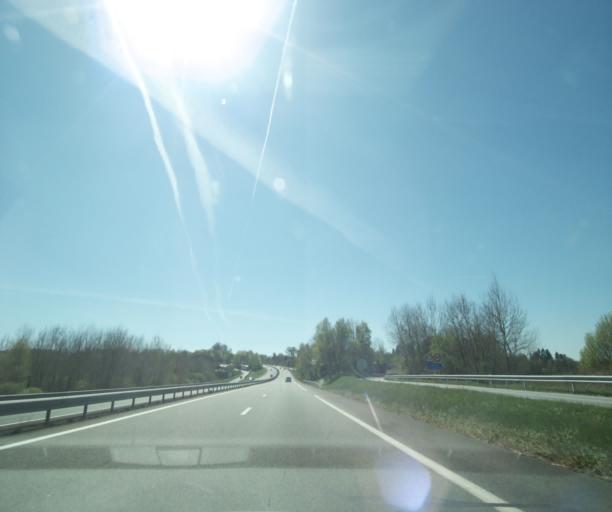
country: FR
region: Limousin
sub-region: Departement de la Haute-Vienne
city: Bessines-sur-Gartempe
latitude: 46.1619
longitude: 1.3768
